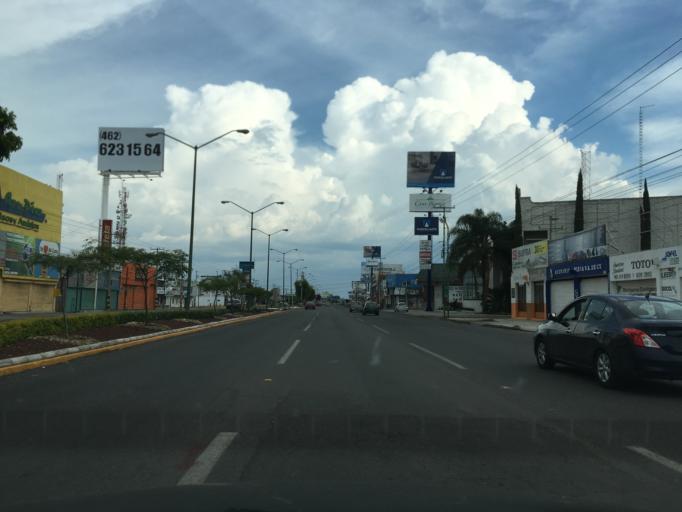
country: MX
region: Guanajuato
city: Celaya
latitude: 20.5498
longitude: -100.8223
